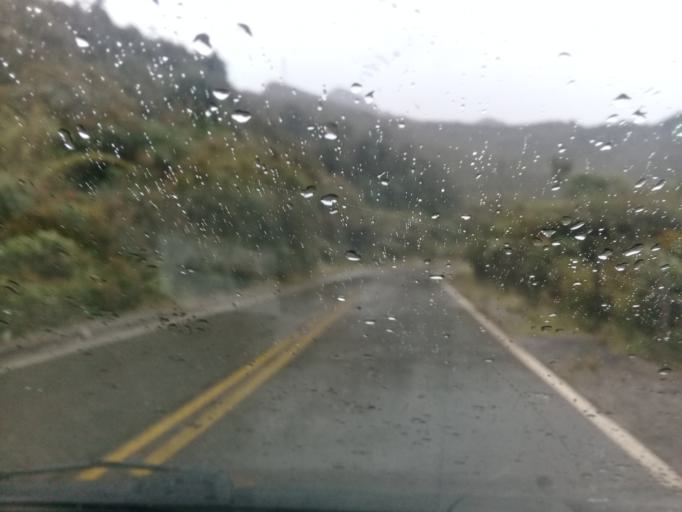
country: CO
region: Cundinamarca
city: Guasca
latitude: 4.8451
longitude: -73.8257
